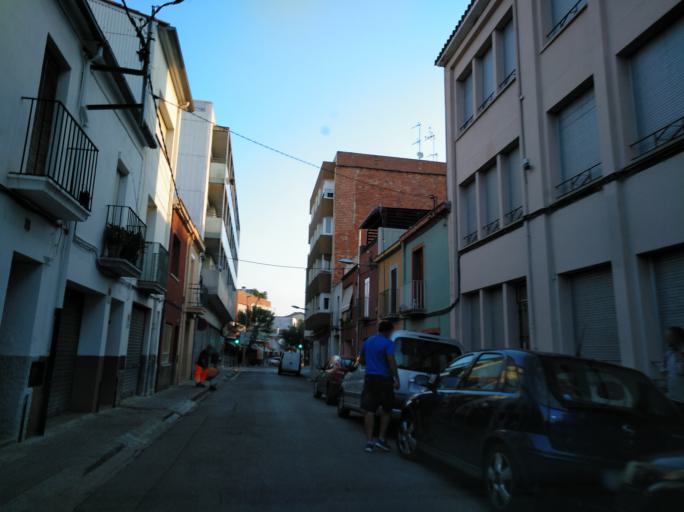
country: ES
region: Catalonia
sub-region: Provincia de Girona
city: Salt
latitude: 41.9753
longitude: 2.7959
